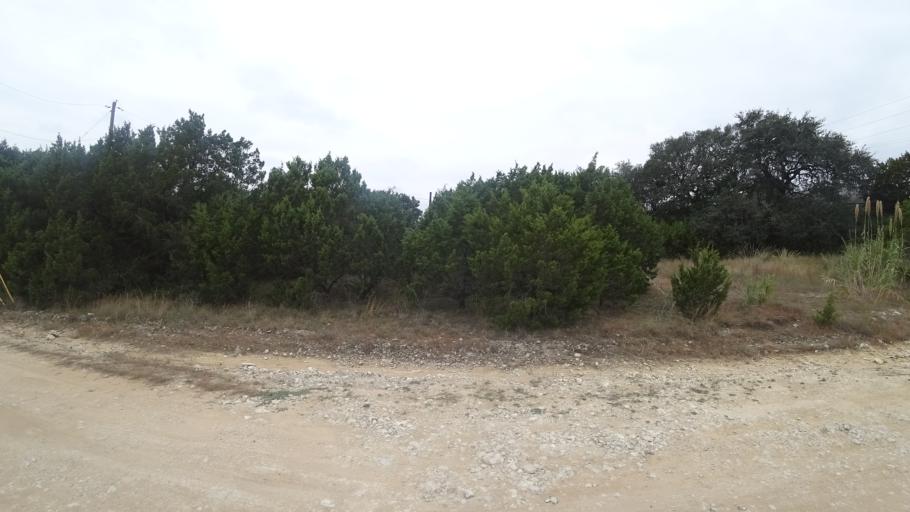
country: US
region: Texas
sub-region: Travis County
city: Lakeway
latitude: 30.3736
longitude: -97.9435
